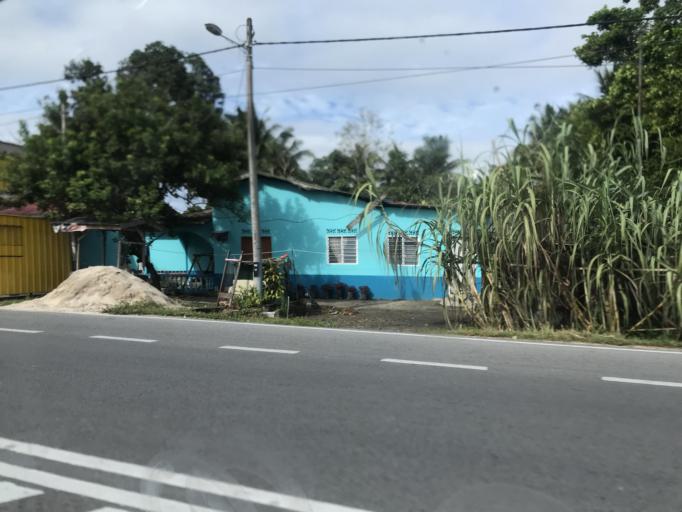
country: MY
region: Kelantan
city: Kota Bharu
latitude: 6.1264
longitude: 102.1810
